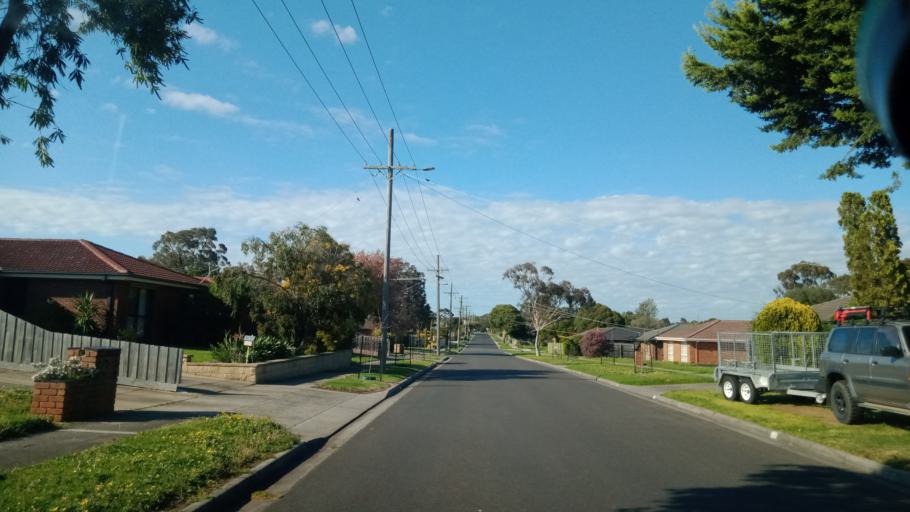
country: AU
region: Victoria
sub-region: Casey
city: Cranbourne West
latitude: -38.0930
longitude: 145.2717
